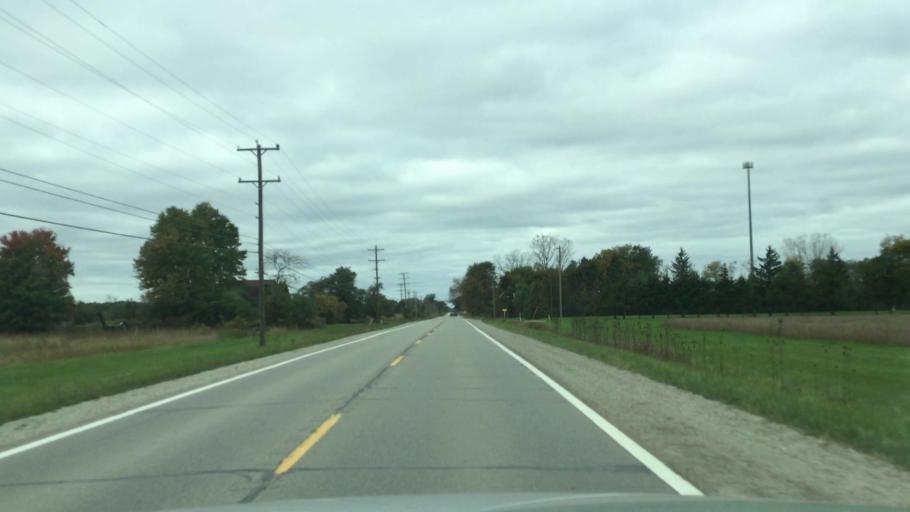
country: US
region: Michigan
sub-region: Macomb County
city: Armada
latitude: 42.8076
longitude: -82.8263
